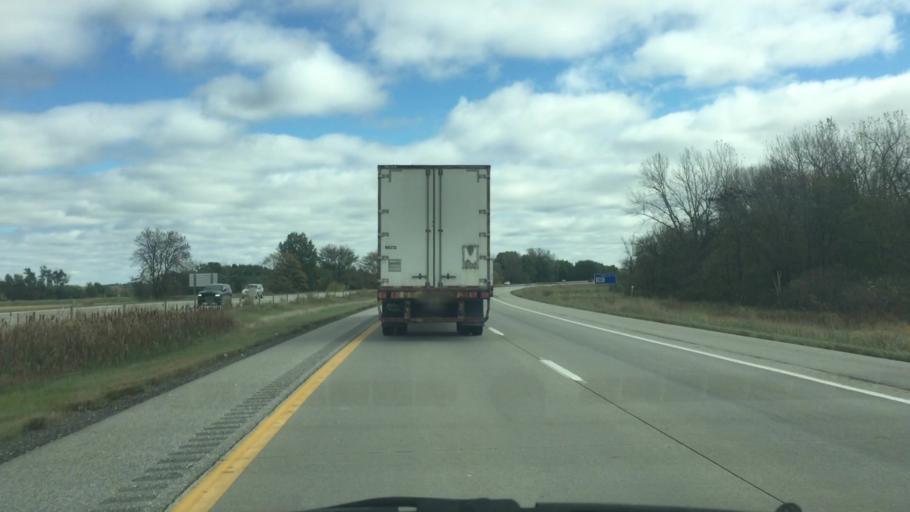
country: US
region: Iowa
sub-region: Jasper County
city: Colfax
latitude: 41.6997
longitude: -93.2067
